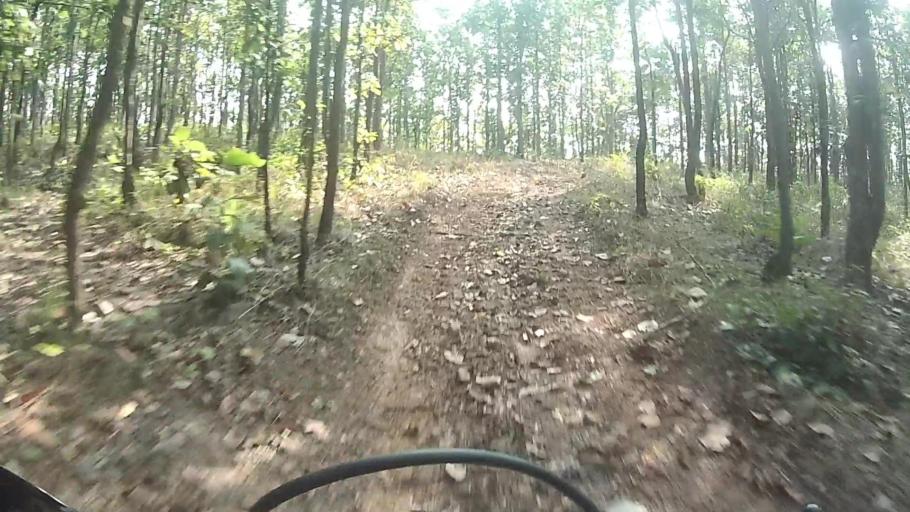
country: TH
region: Chiang Mai
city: San Sai
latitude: 18.9398
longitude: 99.0442
